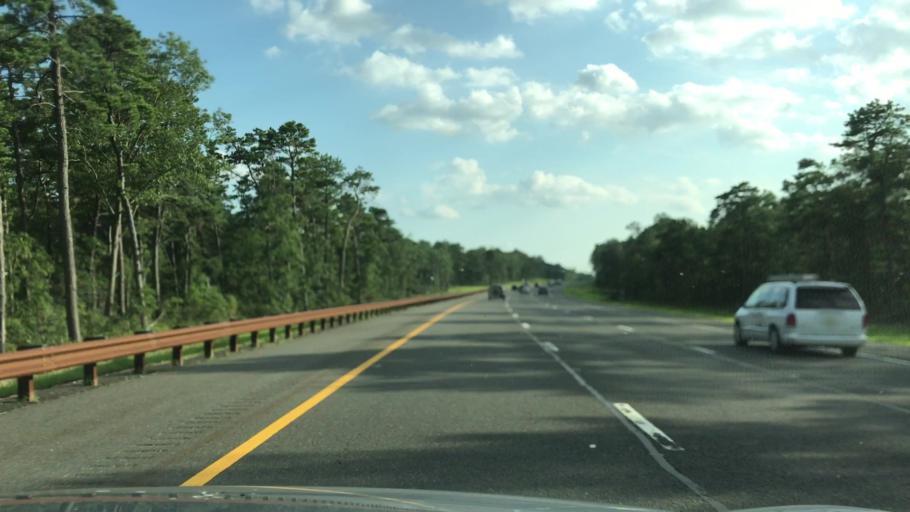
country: US
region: New Jersey
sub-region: Ocean County
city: Manahawkin
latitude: 39.6823
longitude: -74.3046
